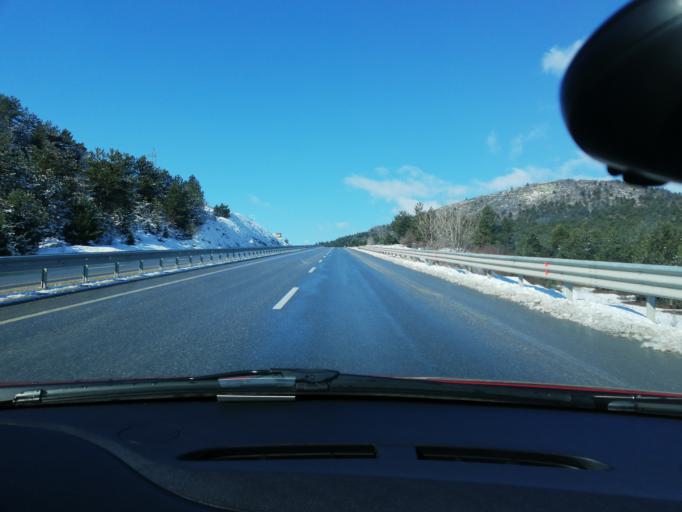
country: TR
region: Kastamonu
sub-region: Cide
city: Kastamonu
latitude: 41.3602
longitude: 33.7019
